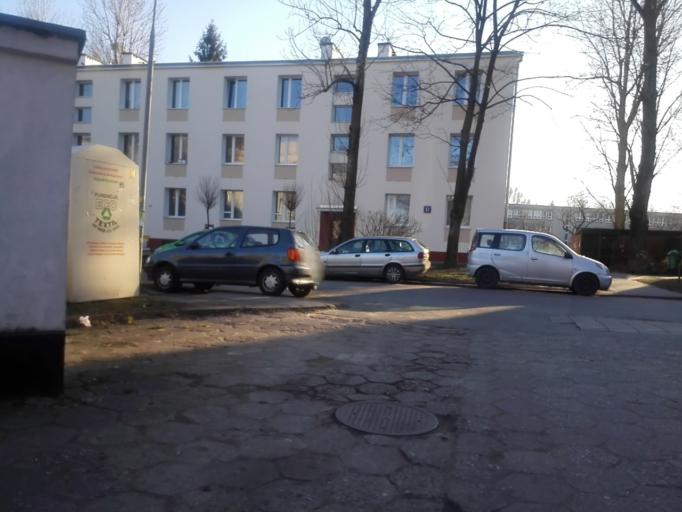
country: PL
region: Masovian Voivodeship
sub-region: Warszawa
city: Mokotow
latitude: 52.1717
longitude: 21.0031
